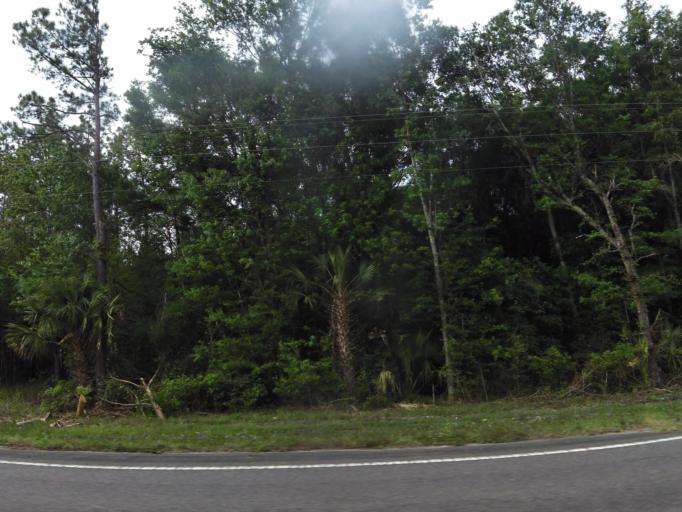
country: US
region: Florida
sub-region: Nassau County
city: Hilliard
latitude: 30.6949
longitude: -81.8540
